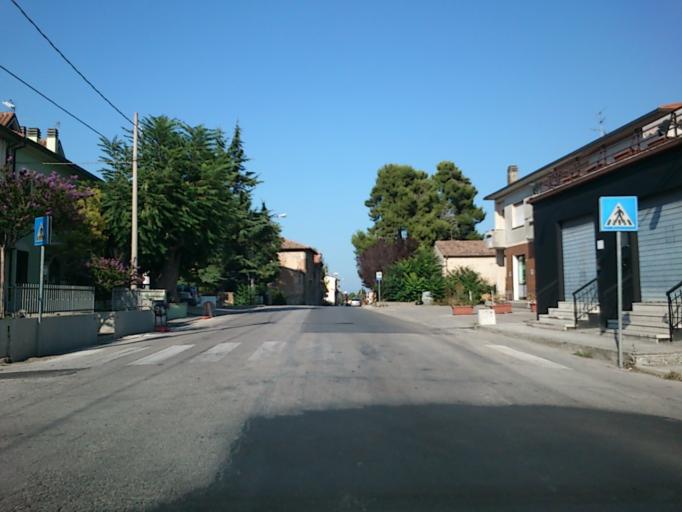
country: IT
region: The Marches
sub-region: Provincia di Pesaro e Urbino
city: Cuccurano
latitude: 43.8021
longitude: 12.9726
